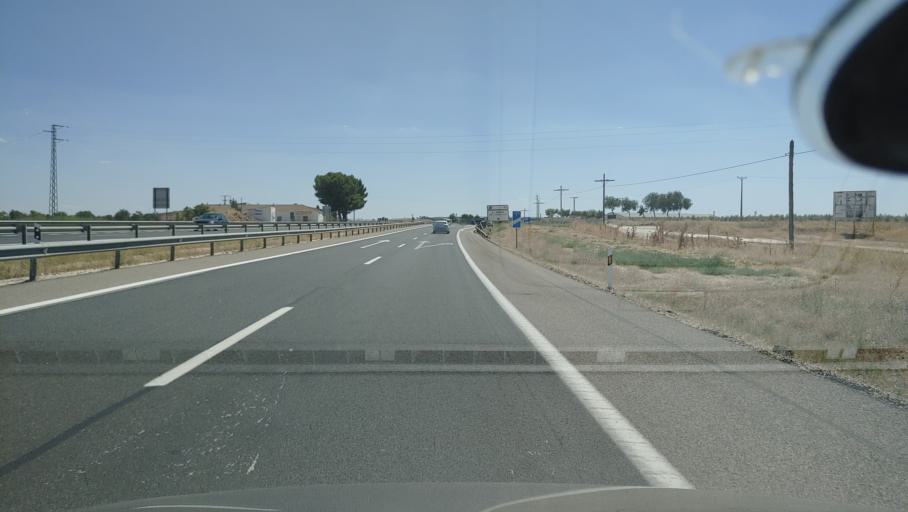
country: ES
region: Castille-La Mancha
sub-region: Provincia de Ciudad Real
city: Villarta de San Juan
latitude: 39.1278
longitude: -3.3785
